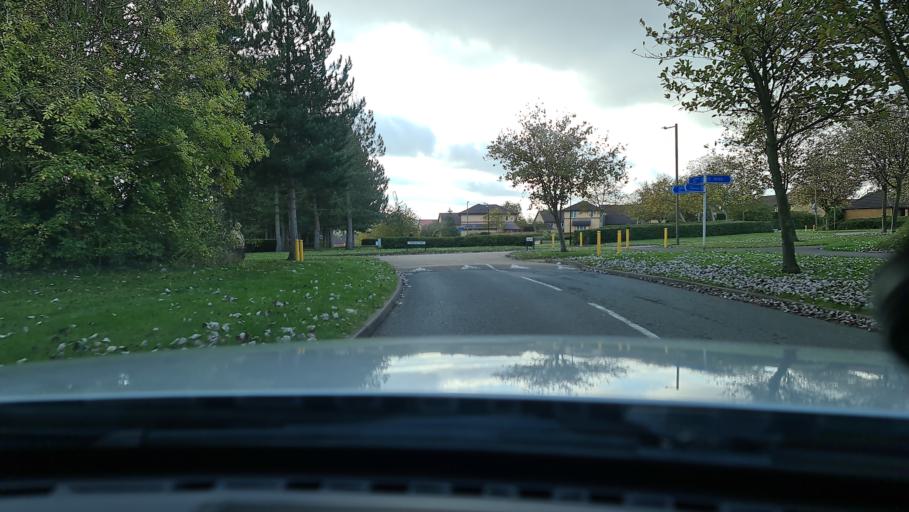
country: GB
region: England
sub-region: Milton Keynes
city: Simpson
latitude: 52.0218
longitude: -0.6929
